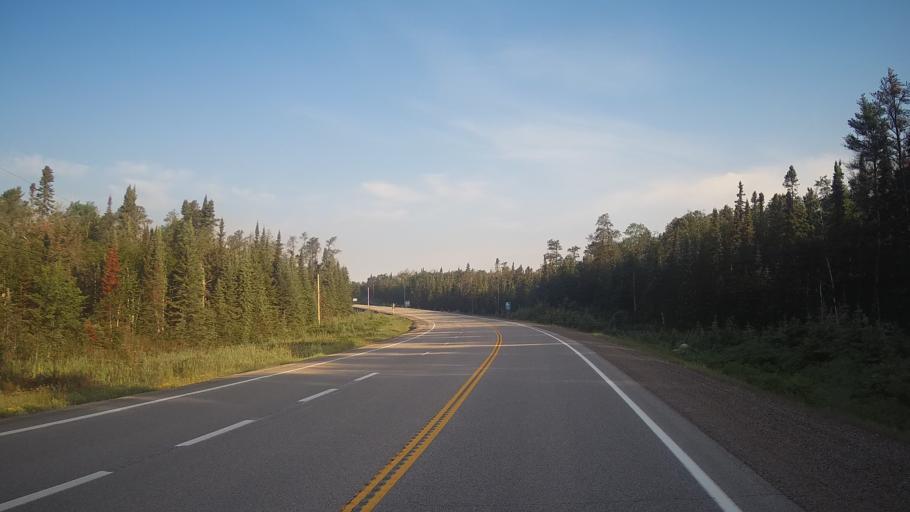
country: CA
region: Ontario
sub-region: Rainy River District
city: Atikokan
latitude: 49.4002
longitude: -91.6151
